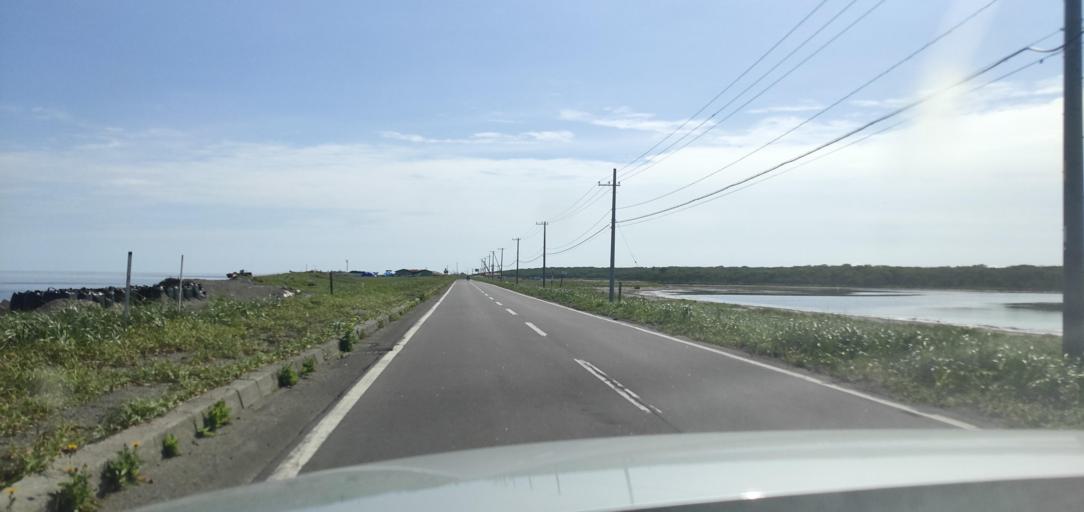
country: JP
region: Hokkaido
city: Shibetsu
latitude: 43.6114
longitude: 145.2648
